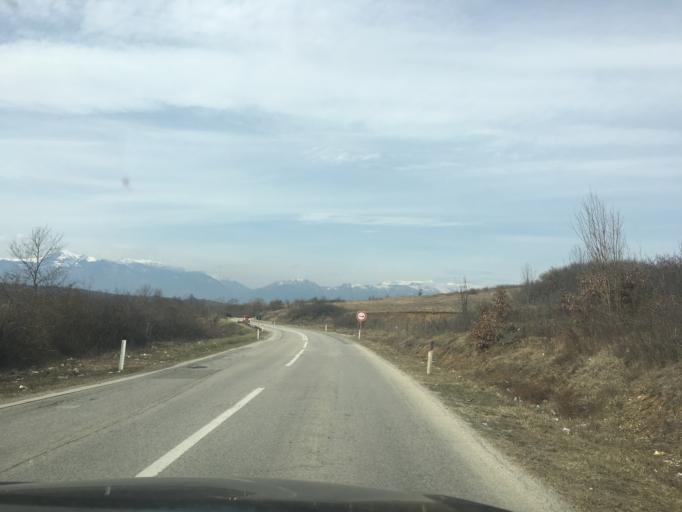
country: XK
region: Pec
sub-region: Komuna e Klines
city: Klina
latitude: 42.5930
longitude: 20.5474
